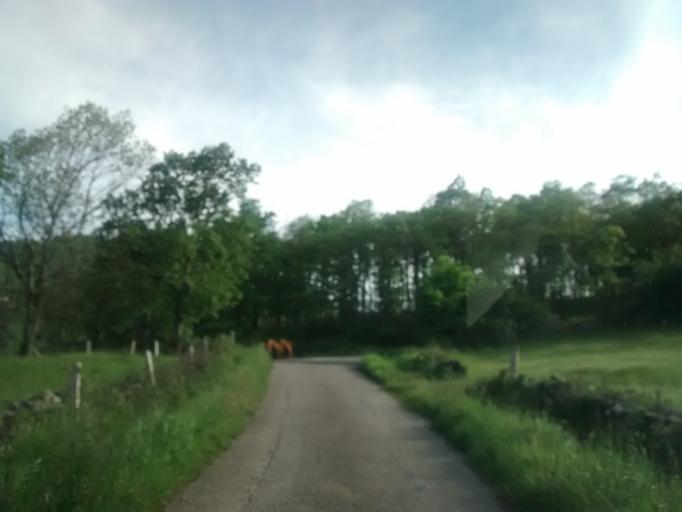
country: ES
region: Cantabria
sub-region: Provincia de Cantabria
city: Potes
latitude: 43.2398
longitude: -4.5627
